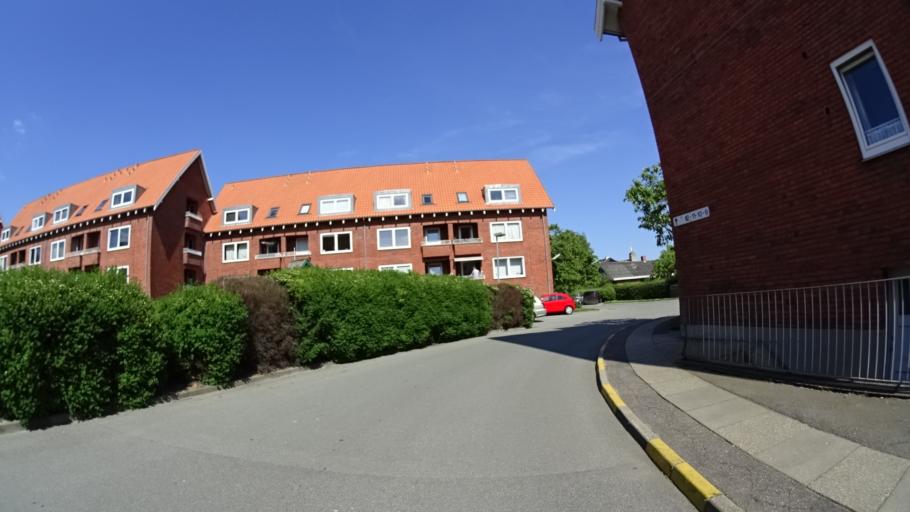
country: DK
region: Central Jutland
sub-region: Arhus Kommune
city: Stavtrup
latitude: 56.1497
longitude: 10.1547
